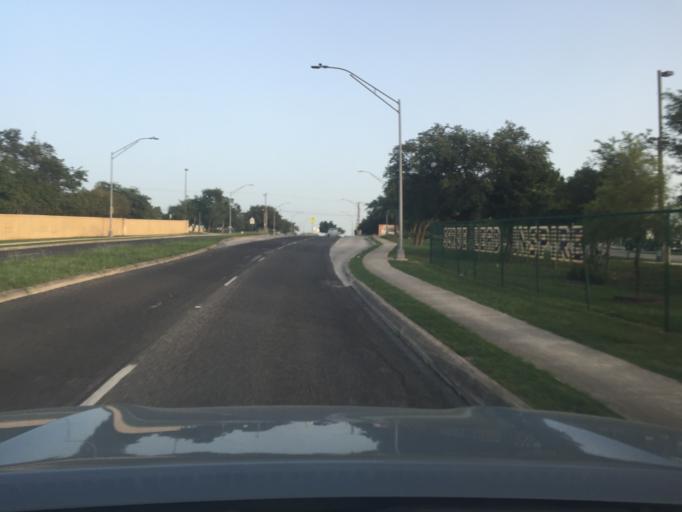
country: US
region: Texas
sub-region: Bexar County
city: Timberwood Park
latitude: 29.6576
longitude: -98.4966
